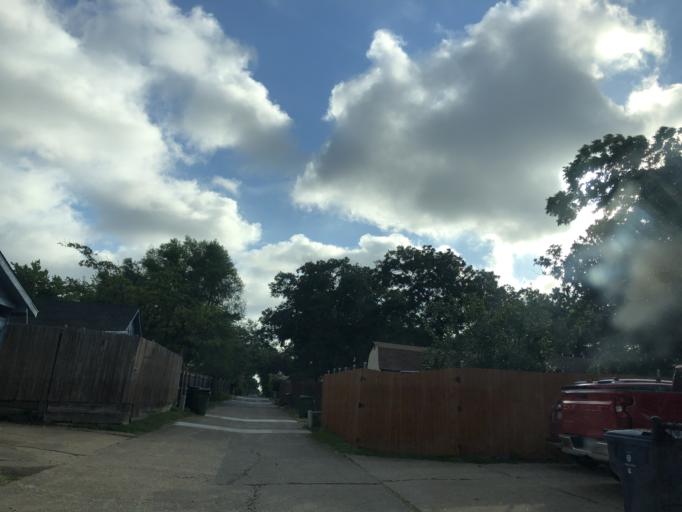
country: US
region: Texas
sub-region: Dallas County
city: Garland
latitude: 32.8528
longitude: -96.6412
